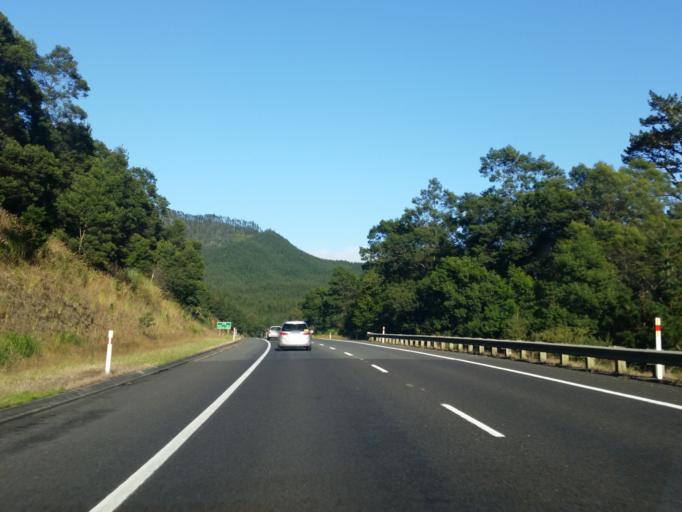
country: NZ
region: Bay of Plenty
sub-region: Western Bay of Plenty District
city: Waihi Beach
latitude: -37.4600
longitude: 175.9200
